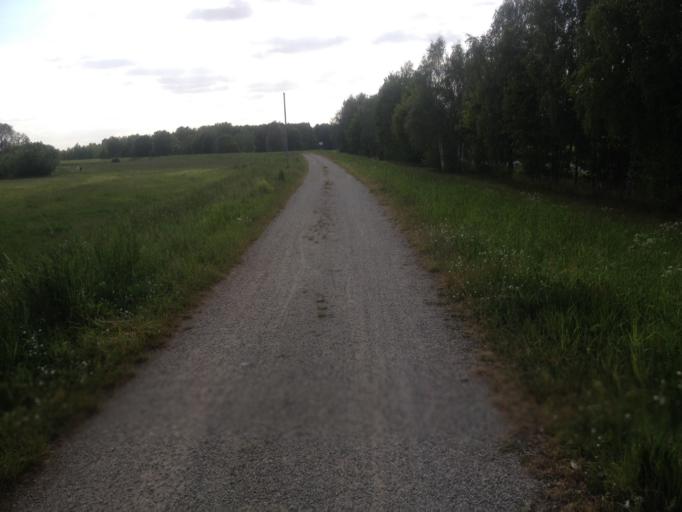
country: DE
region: Brandenburg
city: Drachhausen
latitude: 51.8520
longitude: 14.3105
